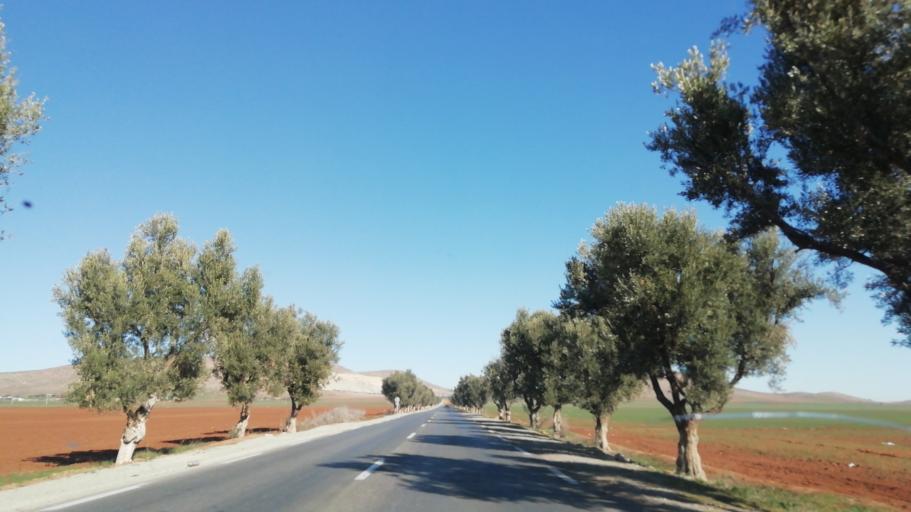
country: DZ
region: Mascara
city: Mascara
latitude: 35.2233
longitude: 0.1137
